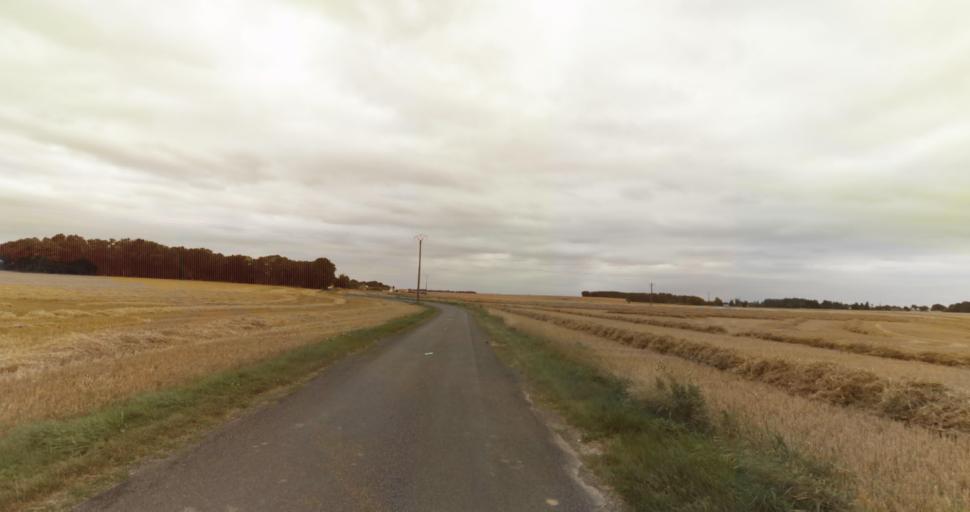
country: FR
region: Haute-Normandie
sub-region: Departement de l'Eure
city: Menilles
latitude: 48.9379
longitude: 1.2689
